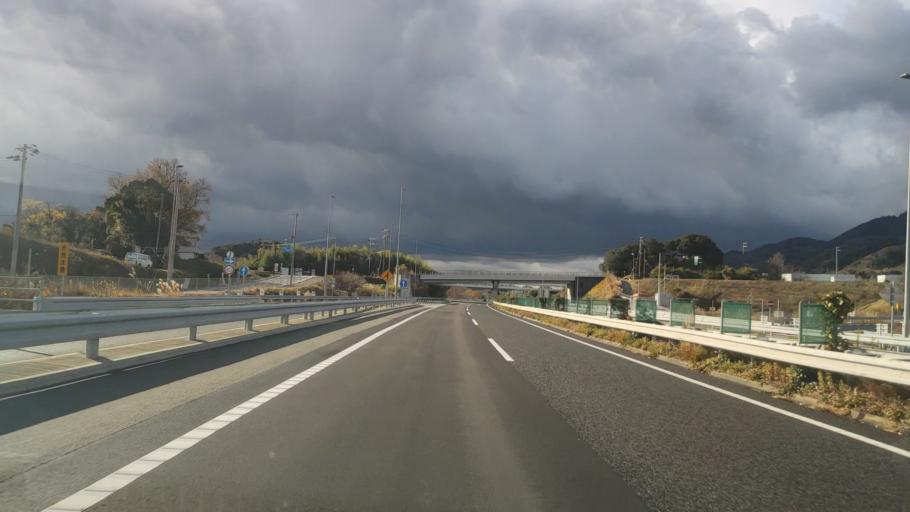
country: JP
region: Hyogo
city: Sumoto
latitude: 34.3737
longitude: 134.8607
